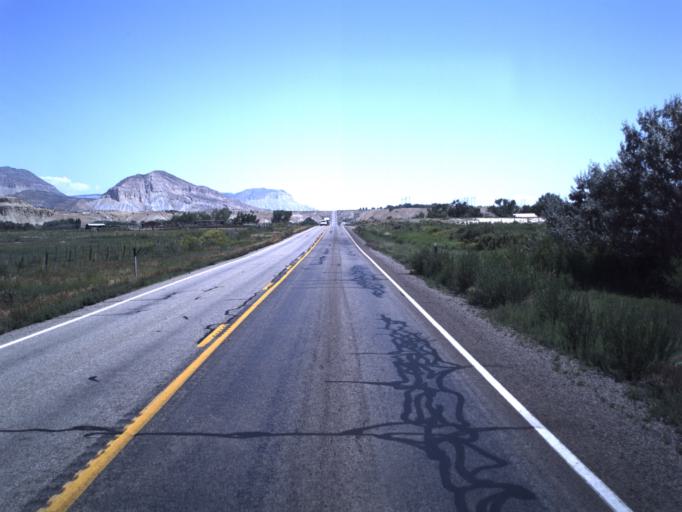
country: US
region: Utah
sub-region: Emery County
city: Ferron
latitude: 38.8677
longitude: -111.2967
